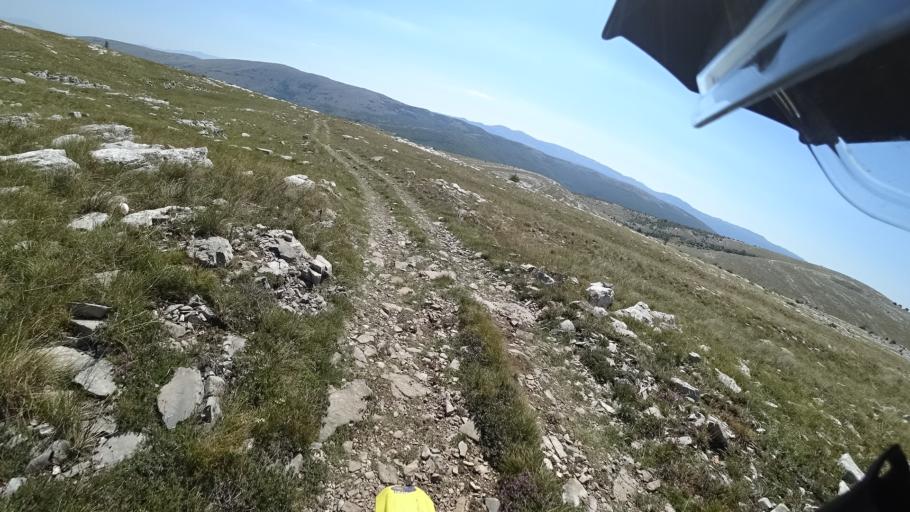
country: HR
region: Splitsko-Dalmatinska
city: Hrvace
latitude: 43.9004
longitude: 16.5991
